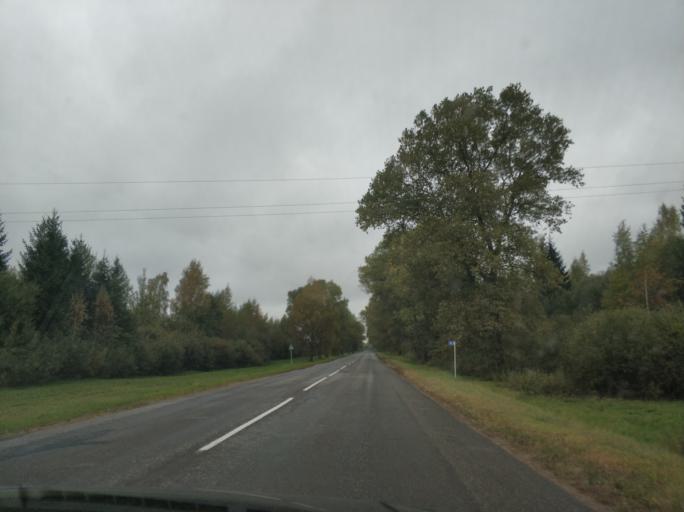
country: BY
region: Vitebsk
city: Polatsk
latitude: 55.4379
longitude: 28.9669
